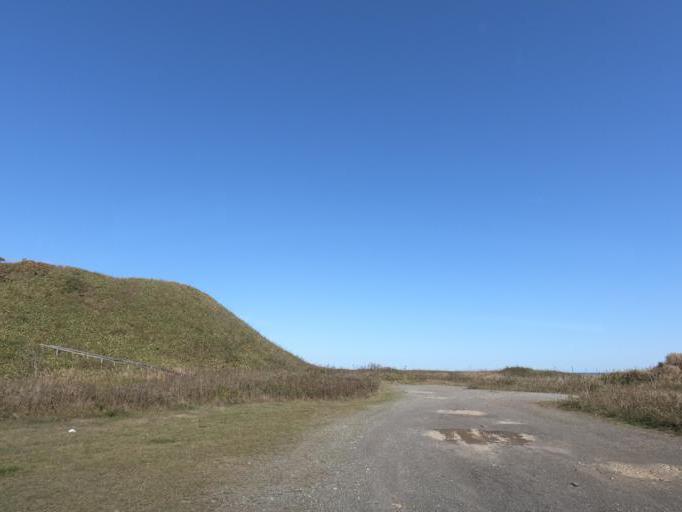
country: JP
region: Hokkaido
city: Obihiro
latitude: 42.6006
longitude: 143.5504
